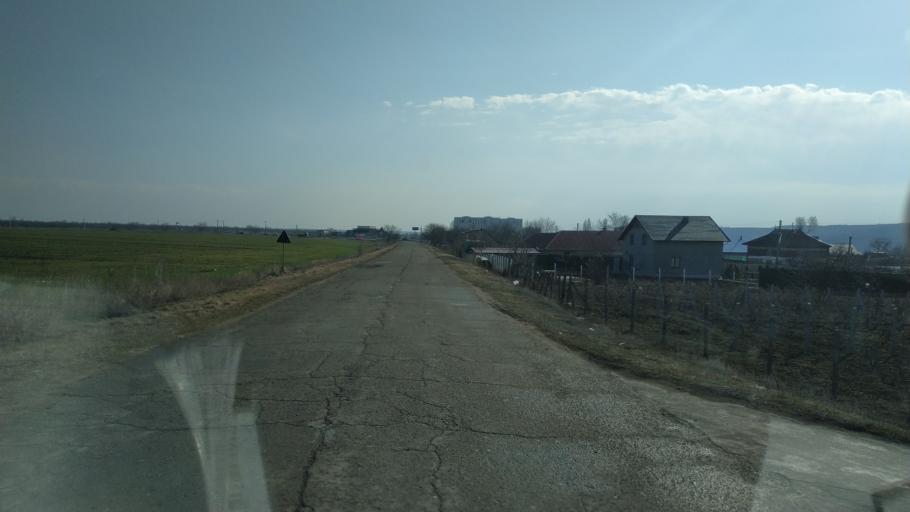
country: MD
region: Chisinau
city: Singera
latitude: 46.6882
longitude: 29.0468
